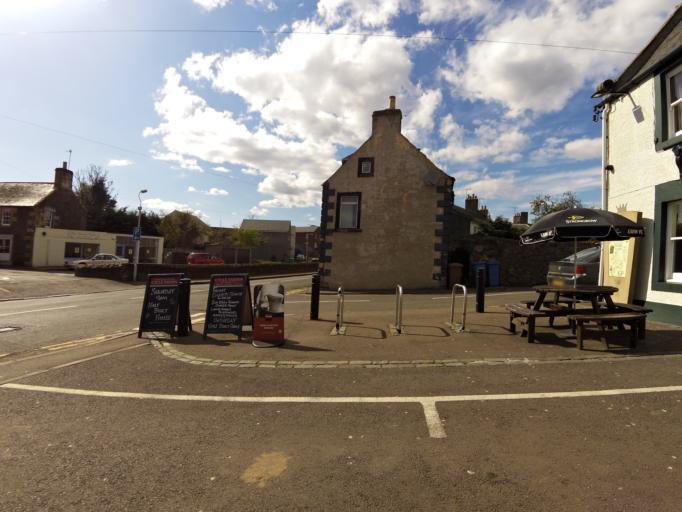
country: GB
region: Scotland
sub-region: Fife
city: Auchtermuchty
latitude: 56.2931
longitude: -3.2323
